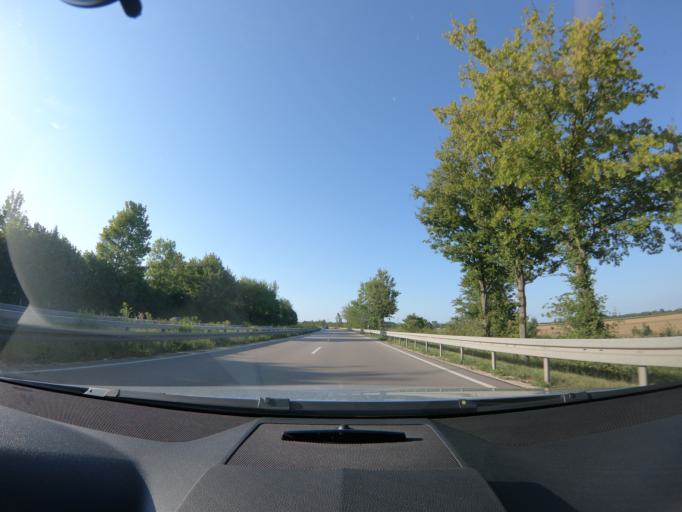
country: DE
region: Bavaria
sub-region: Upper Bavaria
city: Unterschleissheim
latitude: 48.2814
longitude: 11.5905
